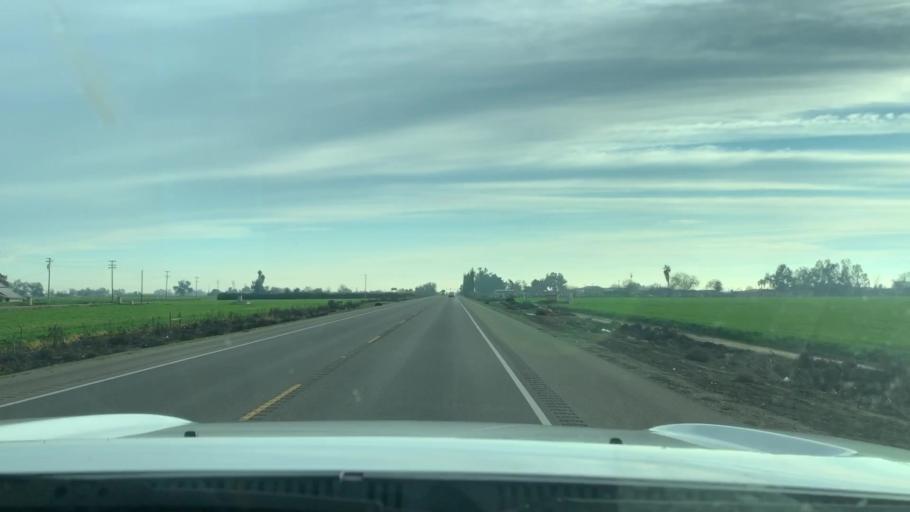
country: US
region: California
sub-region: Fresno County
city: Riverdale
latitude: 36.4415
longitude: -119.7991
